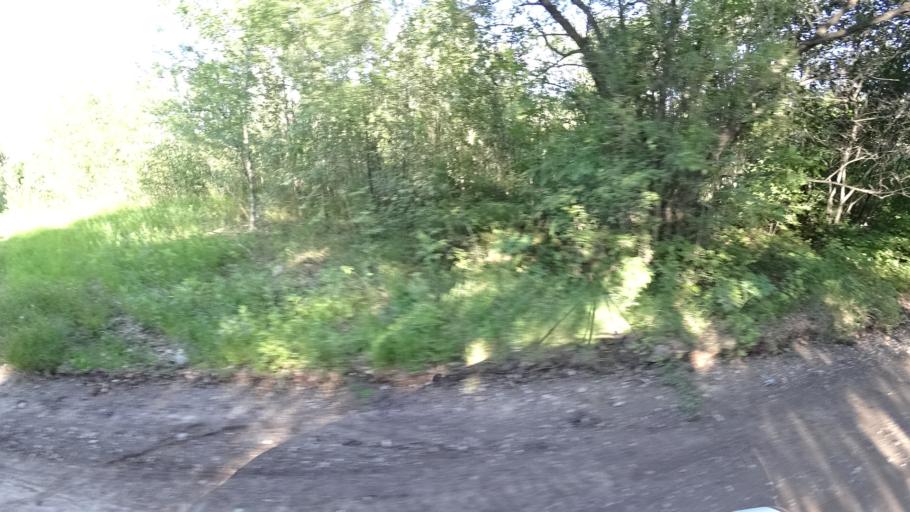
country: RU
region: Khabarovsk Krai
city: Khor
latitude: 47.8505
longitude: 134.9461
